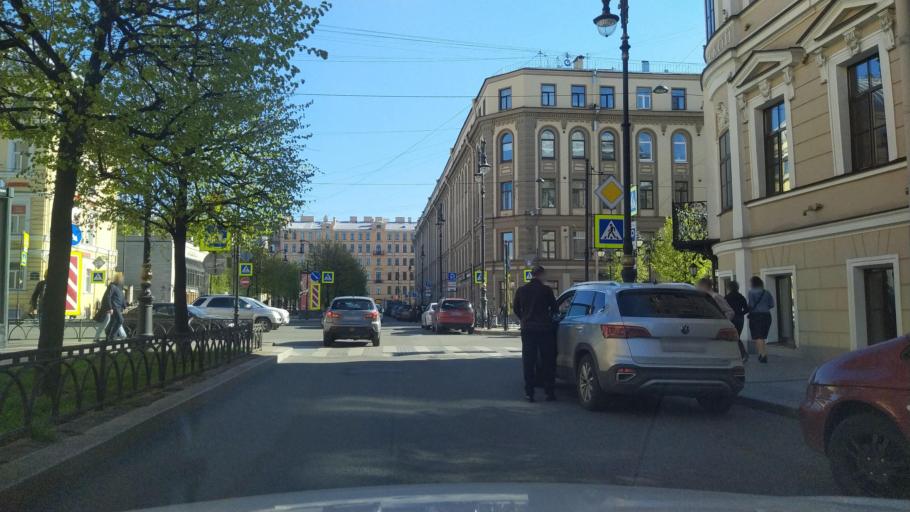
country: RU
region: St.-Petersburg
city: Centralniy
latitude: 59.9456
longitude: 30.3592
